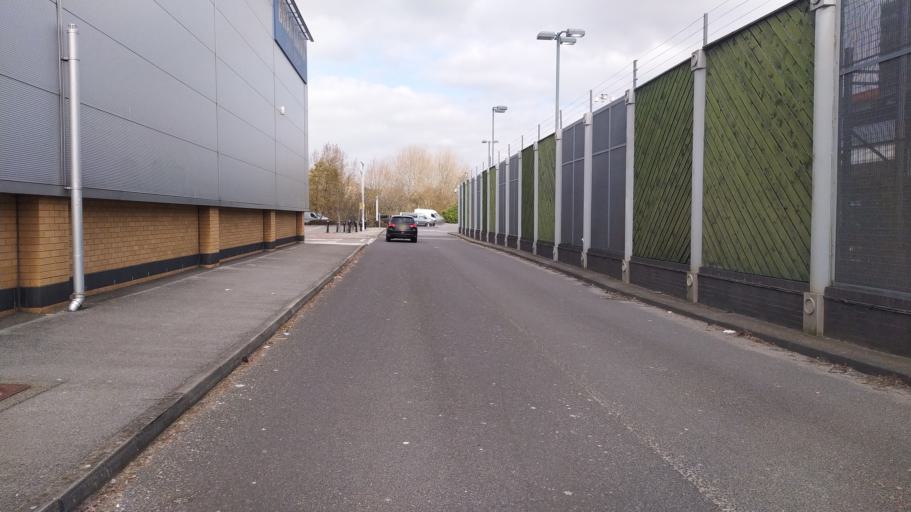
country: GB
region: England
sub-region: Poole
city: Poole
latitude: 50.7358
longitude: -1.9893
